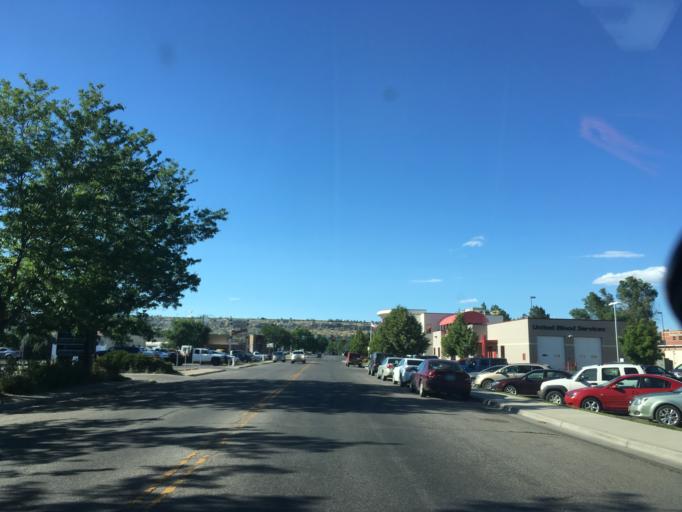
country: US
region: Montana
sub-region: Yellowstone County
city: Billings
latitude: 45.7823
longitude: -108.5538
